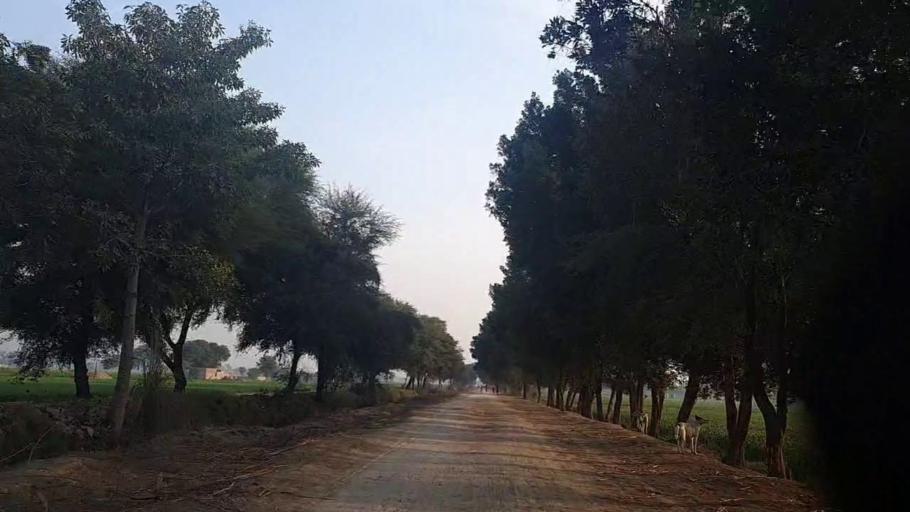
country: PK
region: Sindh
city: Sakrand
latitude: 26.1206
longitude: 68.2315
